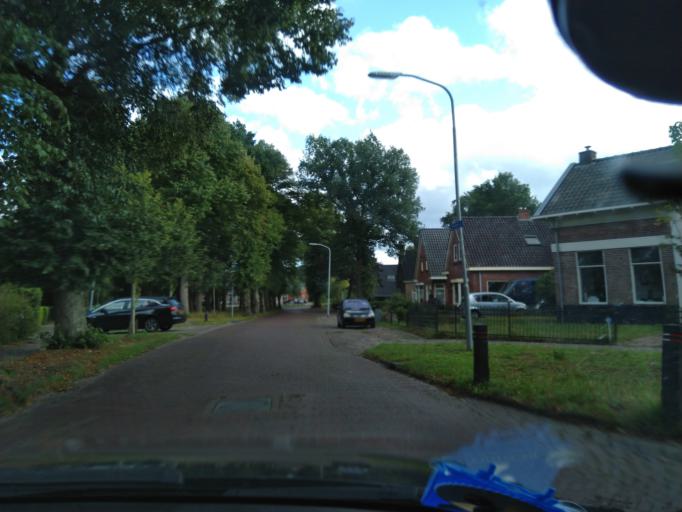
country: NL
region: Drenthe
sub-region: Gemeente Tynaarlo
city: Vries
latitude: 53.0482
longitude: 6.5463
